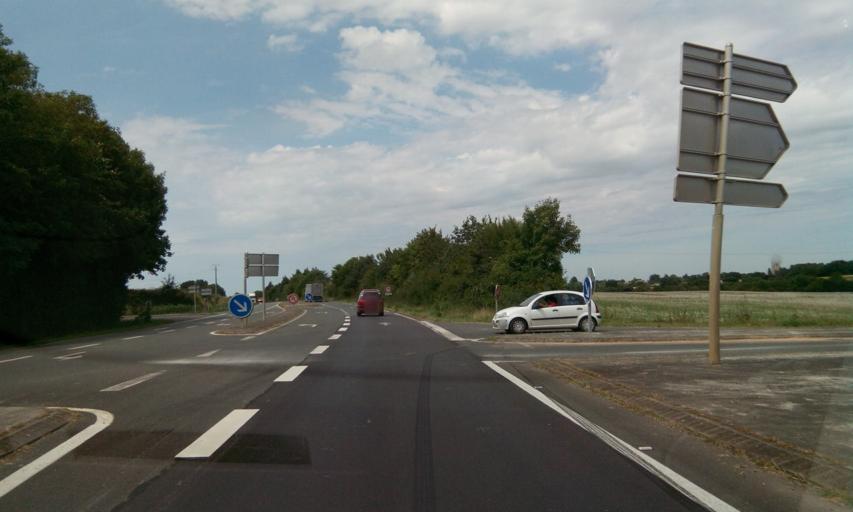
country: FR
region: Poitou-Charentes
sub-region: Departement des Deux-Sevres
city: Celles-sur-Belle
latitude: 46.2524
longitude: -0.1974
